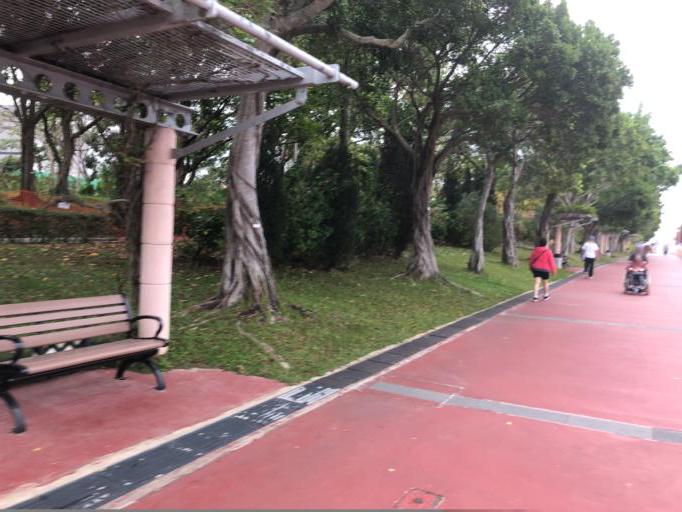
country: HK
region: Tai Po
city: Tai Po
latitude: 22.4521
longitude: 114.1889
